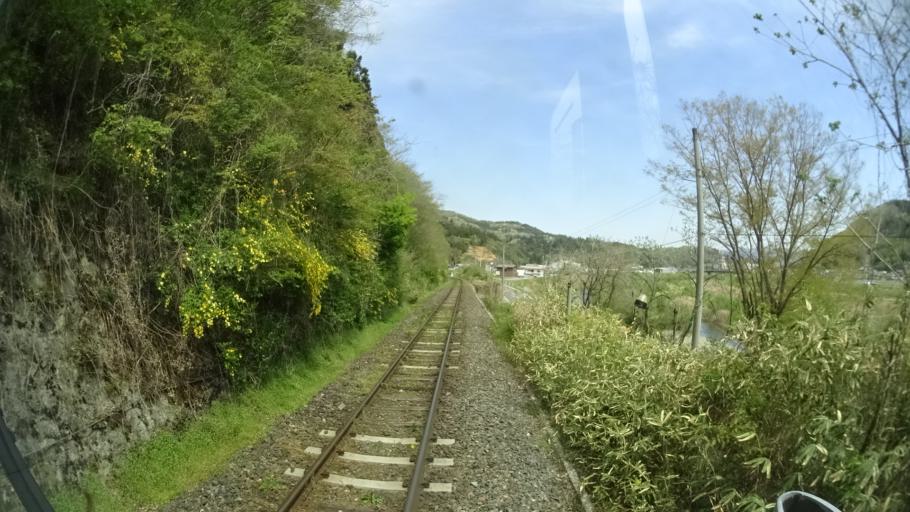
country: JP
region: Iwate
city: Ichinoseki
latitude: 38.9725
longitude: 141.2381
